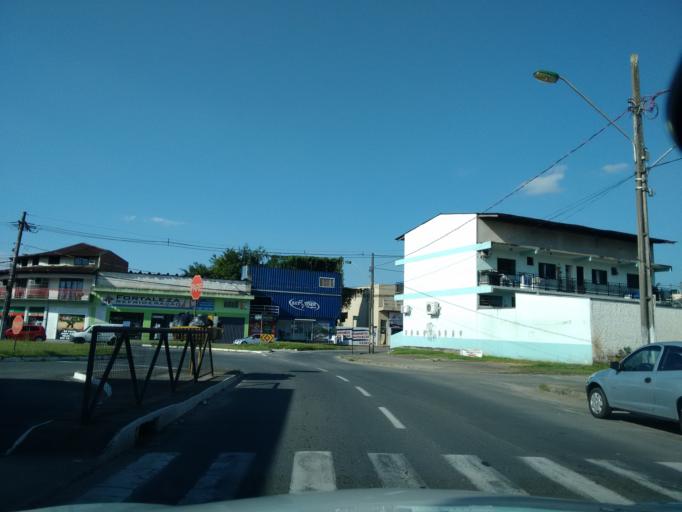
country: BR
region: Santa Catarina
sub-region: Blumenau
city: Blumenau
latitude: -26.8799
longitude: -49.0674
